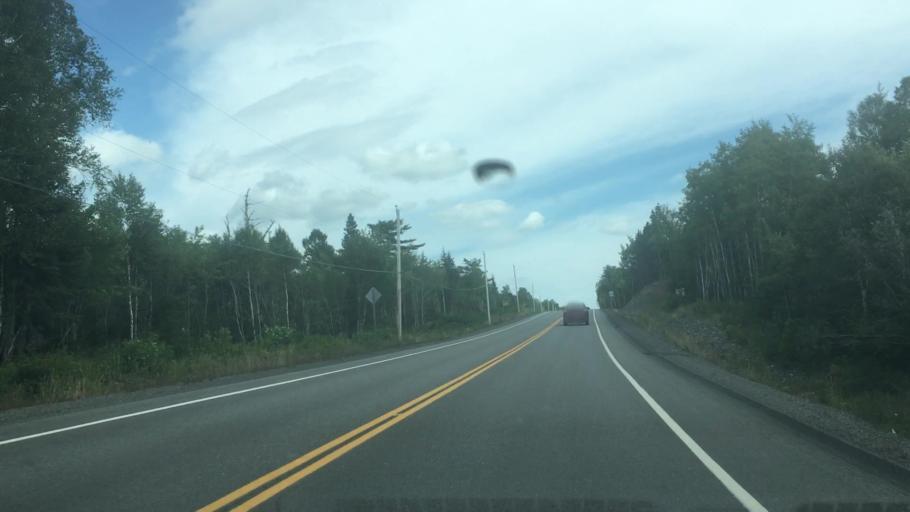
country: CA
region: Nova Scotia
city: Sydney Mines
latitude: 46.3108
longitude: -60.6159
